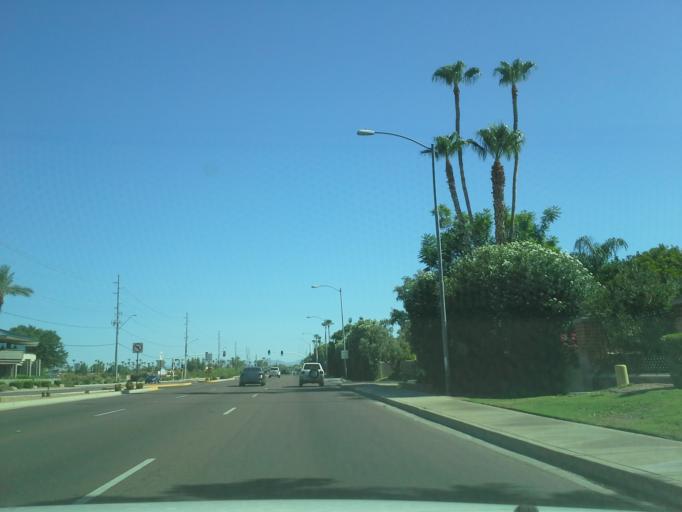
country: US
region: Arizona
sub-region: Maricopa County
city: Paradise Valley
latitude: 33.5334
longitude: -111.9255
